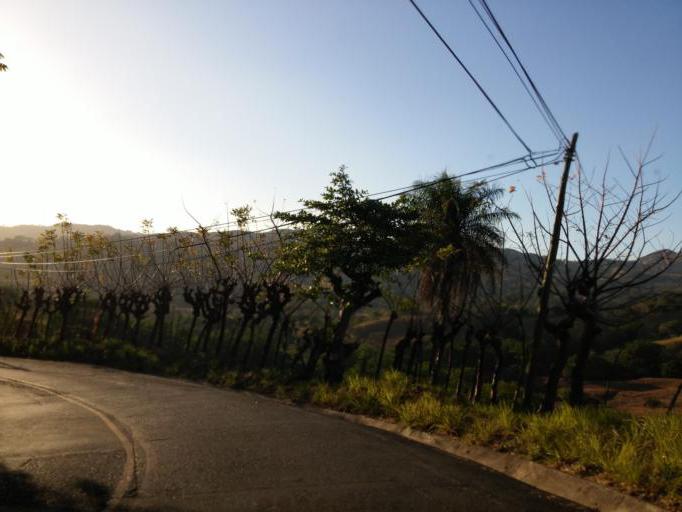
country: CR
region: Alajuela
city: Desamparados
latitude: 9.9553
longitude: -84.4841
